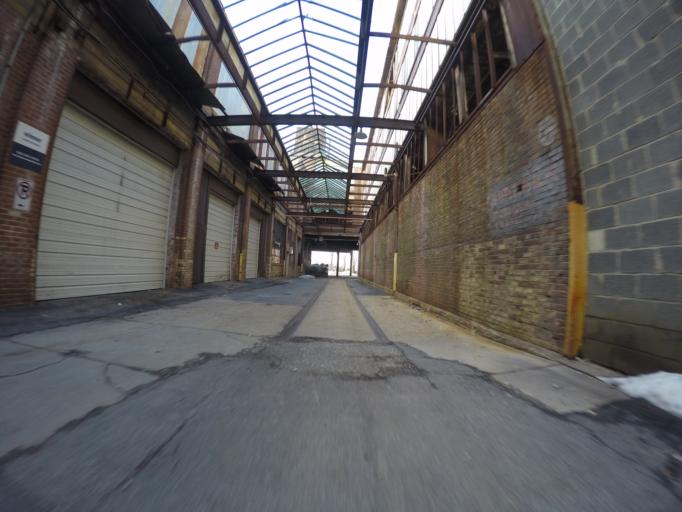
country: US
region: Maryland
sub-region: Baltimore County
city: Dundalk
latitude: 39.2842
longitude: -76.5601
